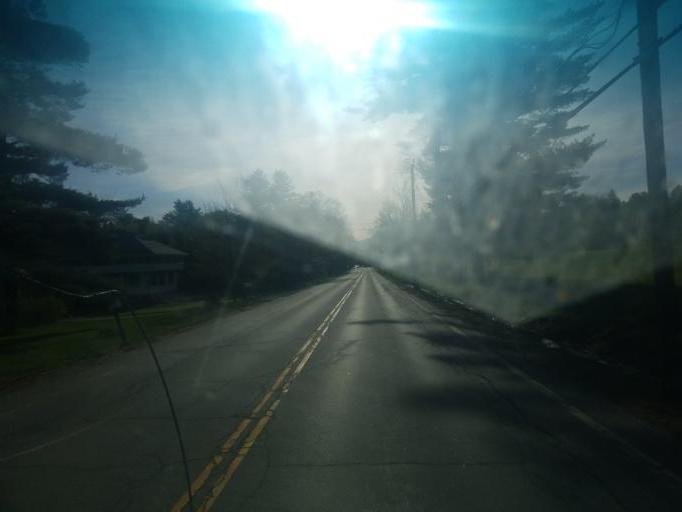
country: US
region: New Hampshire
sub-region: Grafton County
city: Deerfield
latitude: 44.2818
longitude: -71.6598
